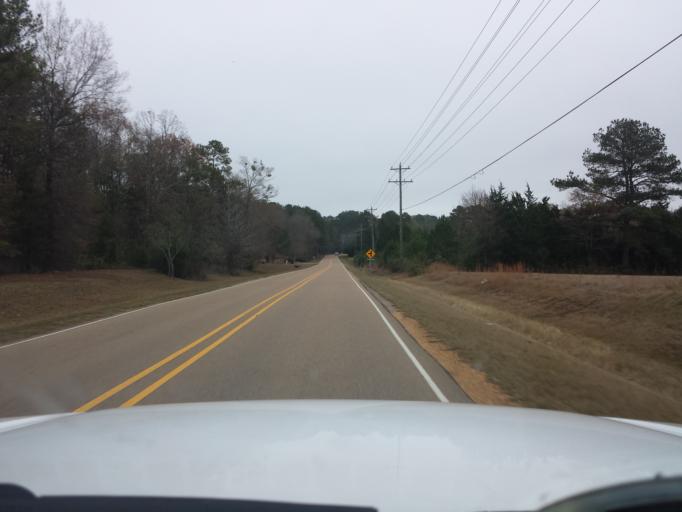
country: US
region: Mississippi
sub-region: Rankin County
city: Brandon
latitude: 32.4214
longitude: -89.9639
